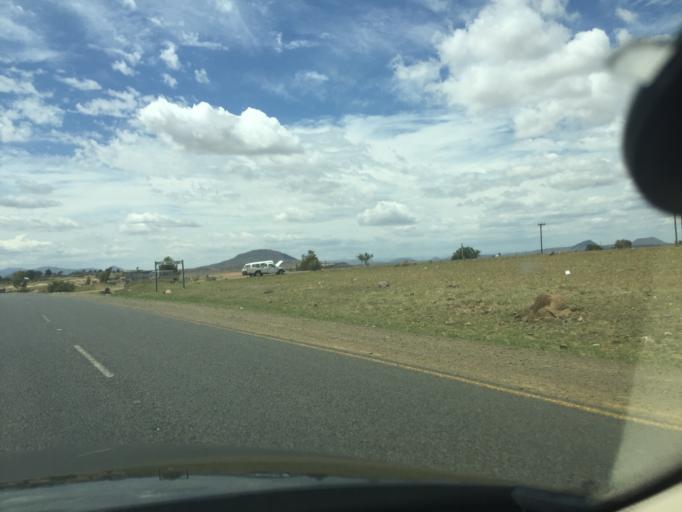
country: LS
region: Mohale's Hoek District
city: Mohale's Hoek
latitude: -30.0090
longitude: 27.3513
